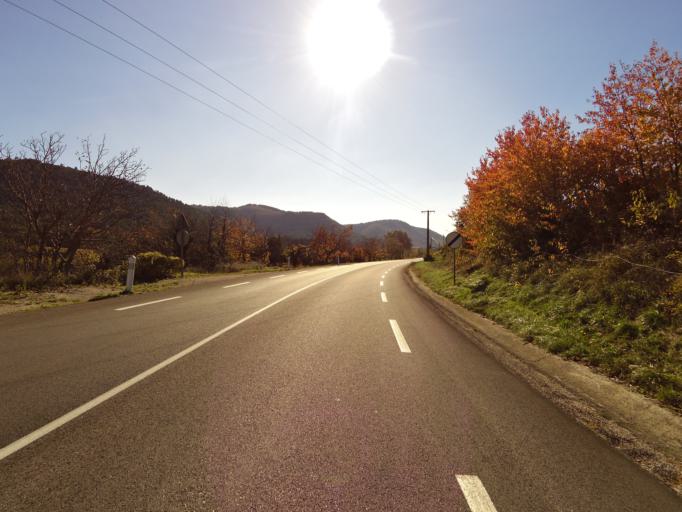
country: FR
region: Rhone-Alpes
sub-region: Departement de l'Ardeche
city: Vesseaux
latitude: 44.6652
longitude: 4.4532
